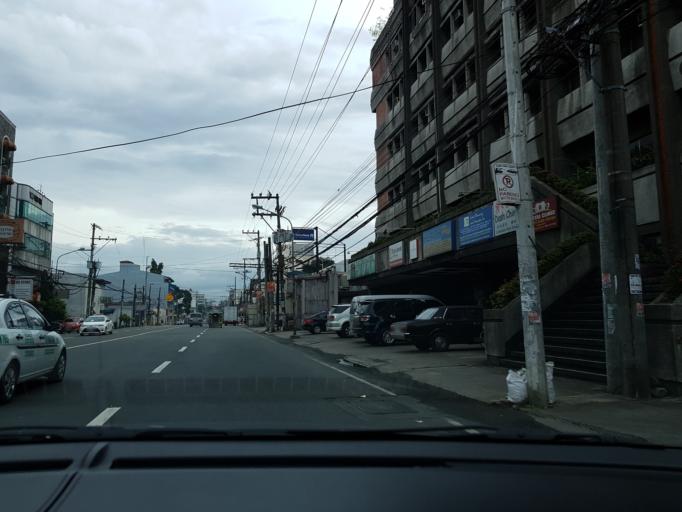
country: PH
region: Calabarzon
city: Del Monte
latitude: 14.6241
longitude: 121.0340
